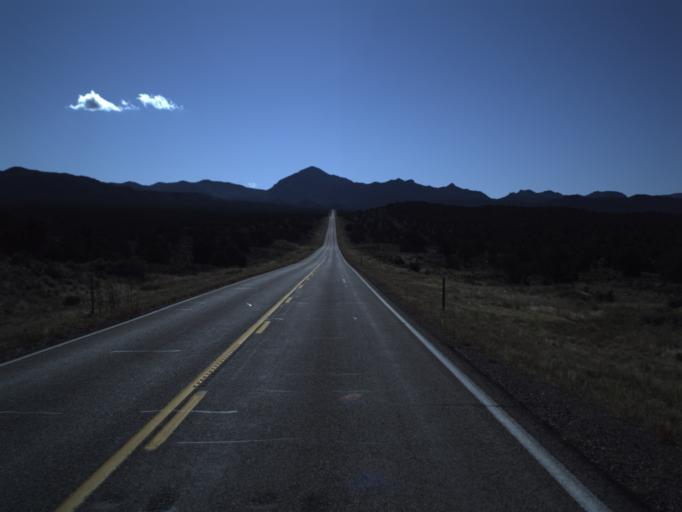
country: US
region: Utah
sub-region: Washington County
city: Enterprise
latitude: 37.6516
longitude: -113.4507
